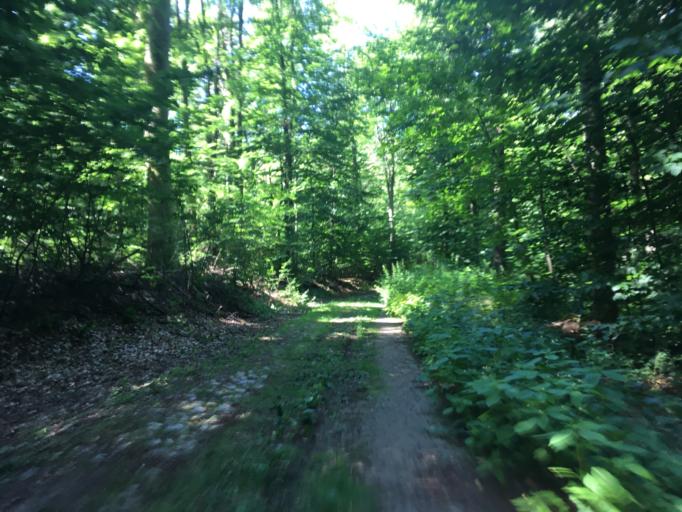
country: DE
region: Brandenburg
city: Grosswoltersdorf
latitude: 53.1428
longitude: 13.0503
